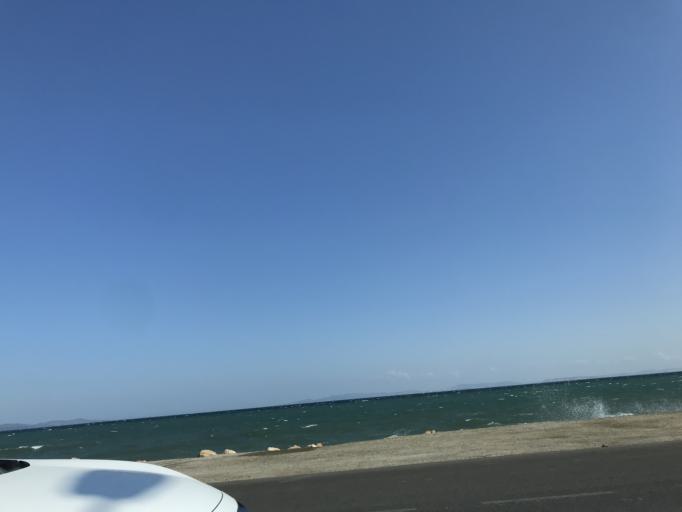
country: TR
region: Izmir
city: Urla
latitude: 38.3743
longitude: 26.8684
